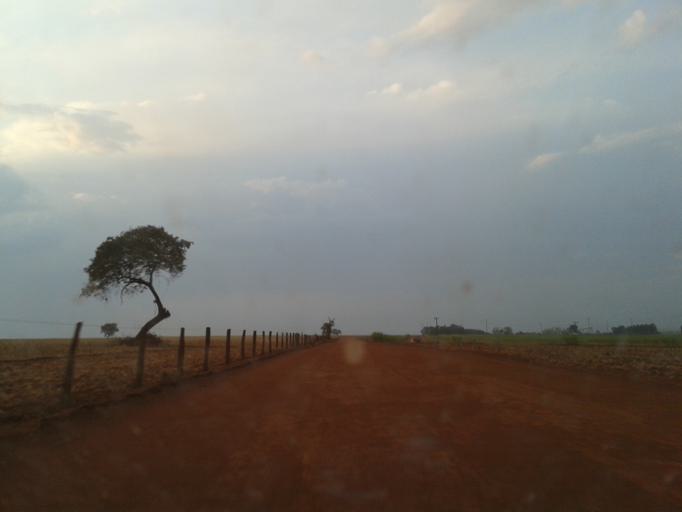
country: BR
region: Minas Gerais
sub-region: Capinopolis
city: Capinopolis
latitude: -18.7180
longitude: -49.6852
